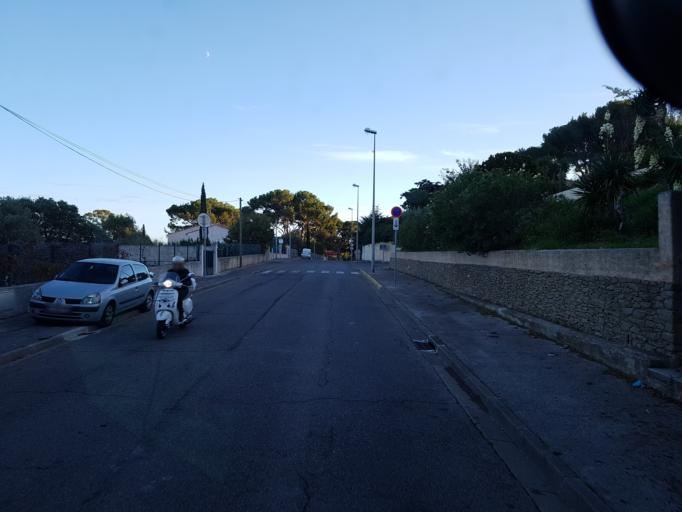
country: FR
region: Provence-Alpes-Cote d'Azur
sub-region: Departement des Bouches-du-Rhone
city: La Ciotat
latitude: 43.1737
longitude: 5.5984
